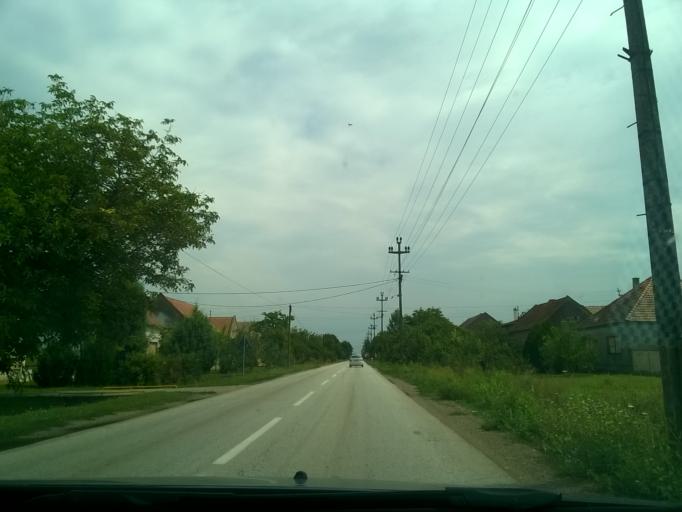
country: RS
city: Sutjeska
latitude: 45.3802
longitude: 20.6937
